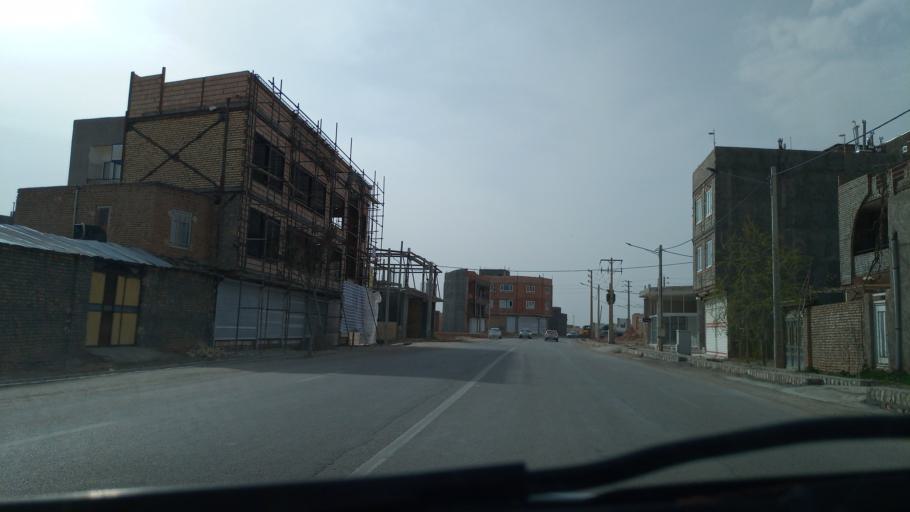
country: IR
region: Khorasan-e Shomali
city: Esfarayen
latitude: 37.0830
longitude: 57.5073
